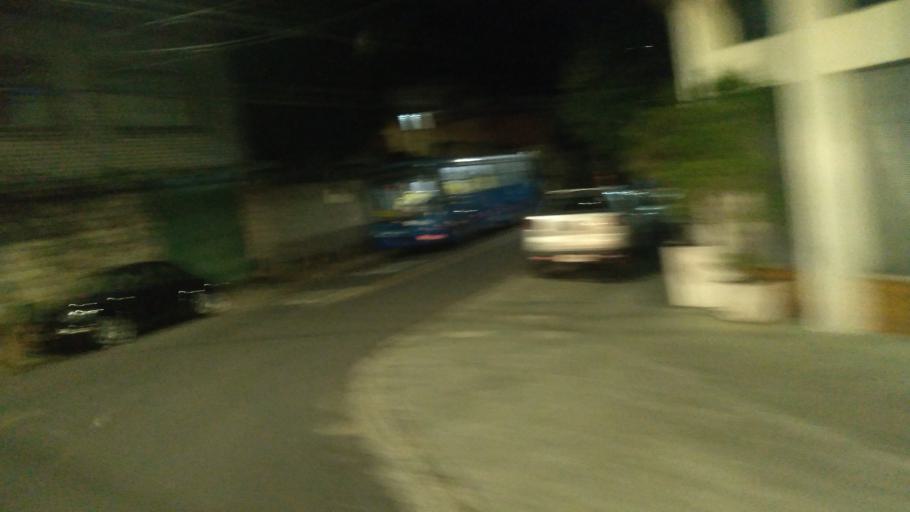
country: BR
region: Minas Gerais
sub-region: Belo Horizonte
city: Belo Horizonte
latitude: -19.9093
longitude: -43.9509
